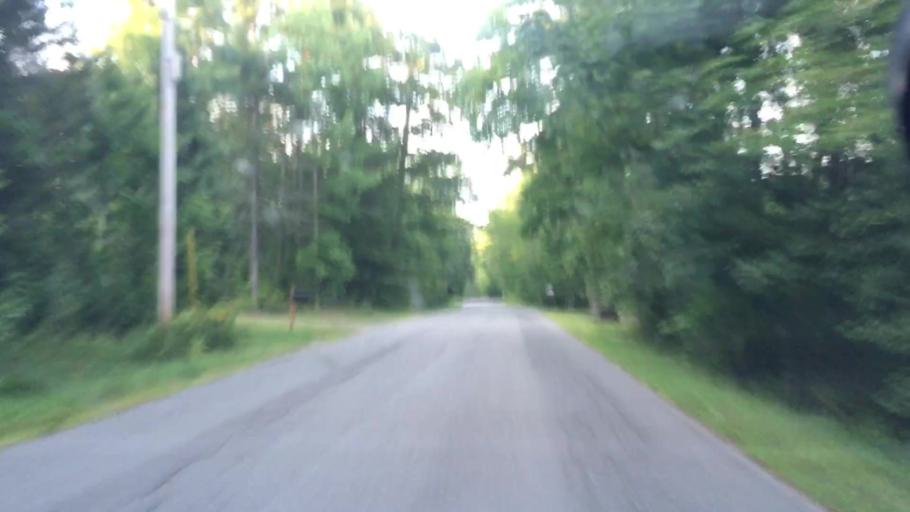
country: US
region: Maine
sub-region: Waldo County
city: Frankfort
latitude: 44.6633
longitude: -68.9276
